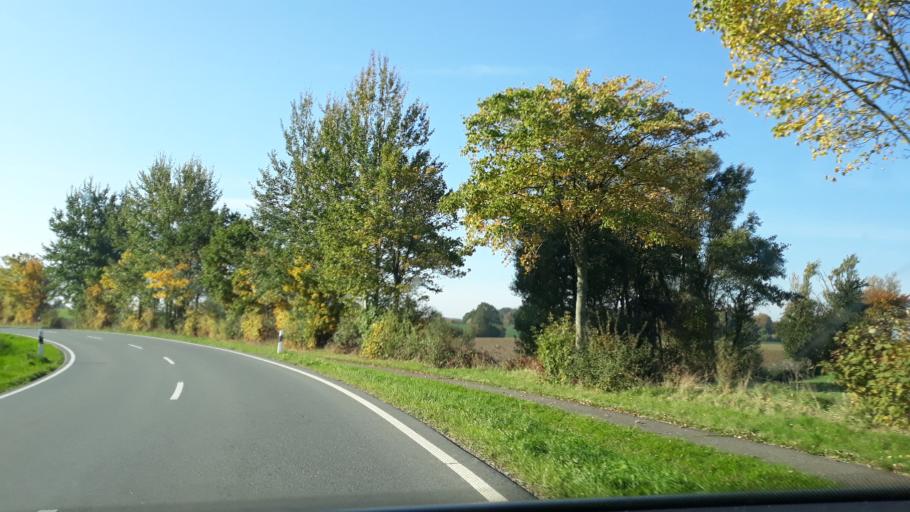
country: DE
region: Schleswig-Holstein
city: Ulsby
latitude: 54.6224
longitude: 9.5952
